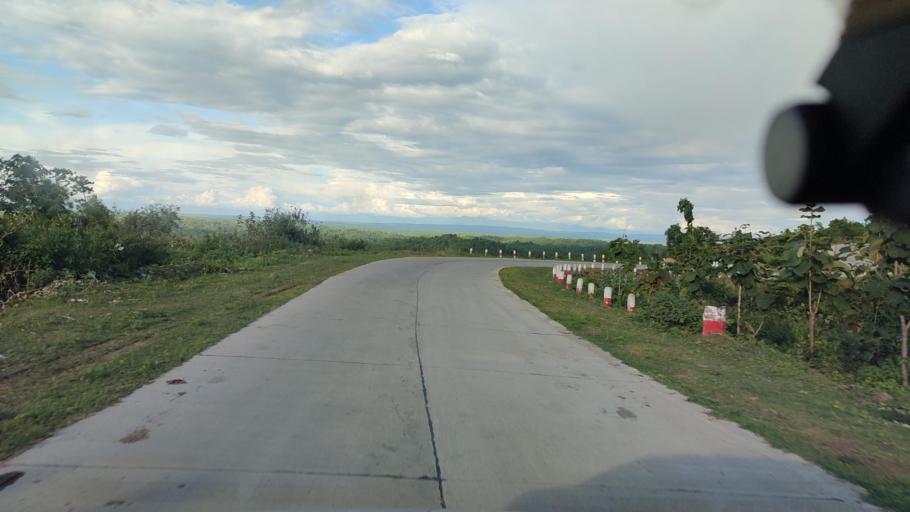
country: MM
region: Magway
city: Taungdwingyi
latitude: 20.0235
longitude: 95.8237
